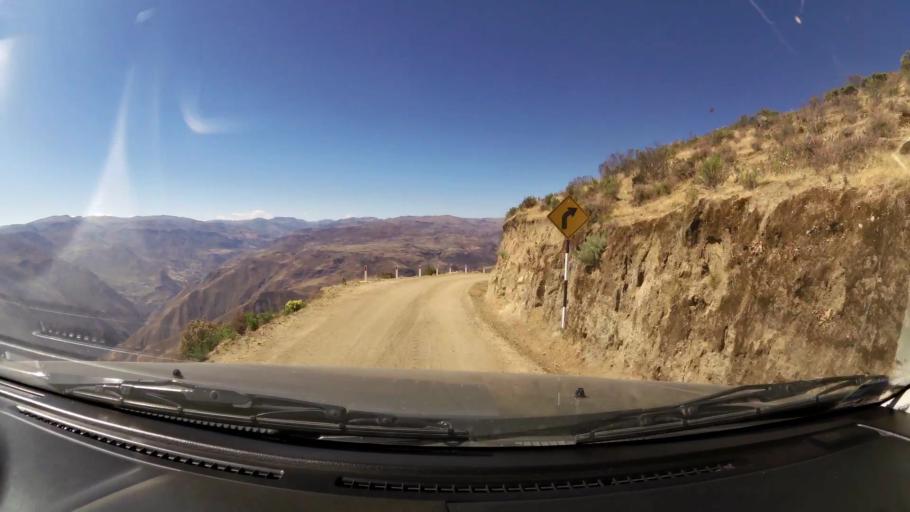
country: PE
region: Huancavelica
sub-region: Huaytara
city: Quito-Arma
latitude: -13.6244
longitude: -75.3530
